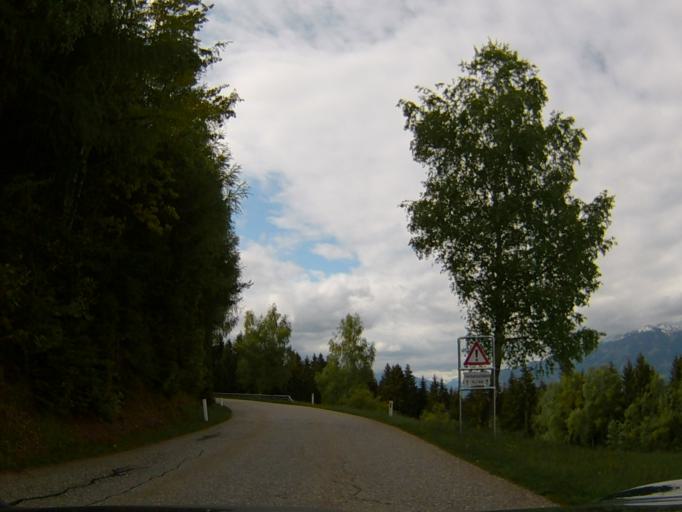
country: AT
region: Carinthia
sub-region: Politischer Bezirk Villach Land
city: Stockenboi
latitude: 46.7327
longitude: 13.5782
